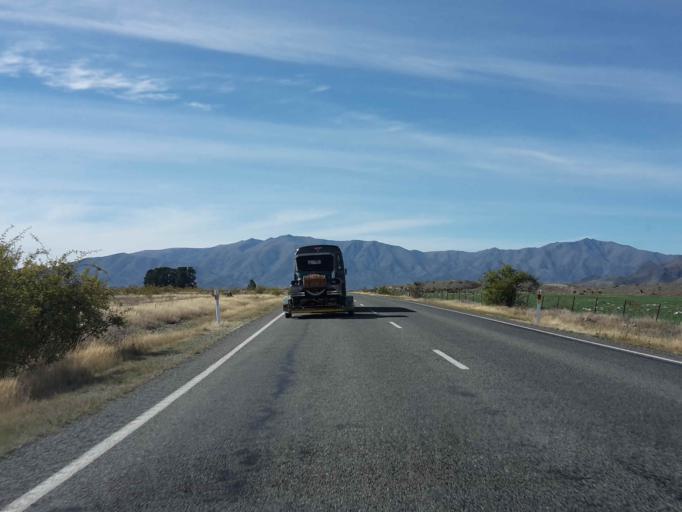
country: NZ
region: Otago
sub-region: Queenstown-Lakes District
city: Wanaka
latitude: -44.5121
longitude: 169.8434
